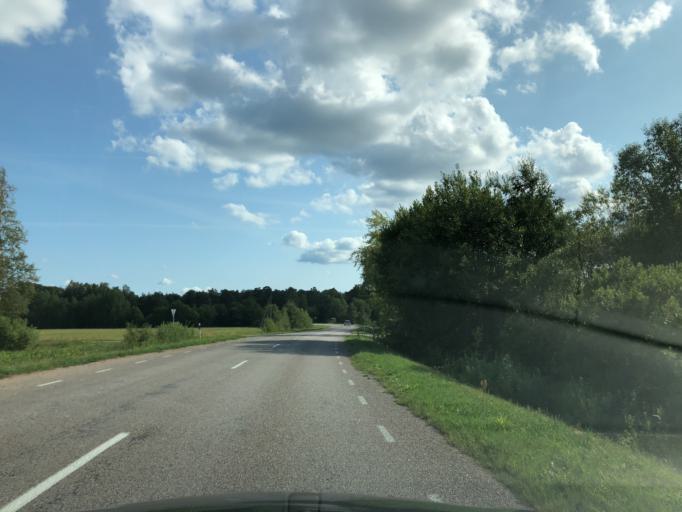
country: EE
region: Hiiumaa
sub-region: Kaerdla linn
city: Kardla
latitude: 58.7107
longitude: 22.5868
